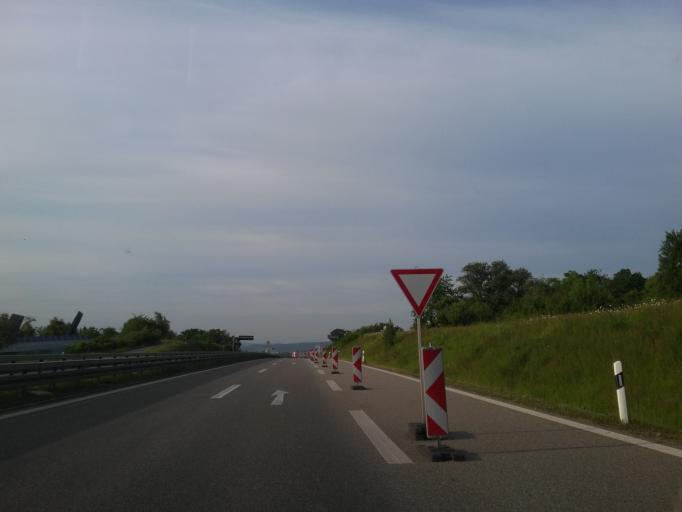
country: DE
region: Baden-Wuerttemberg
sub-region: Regierungsbezirk Stuttgart
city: Leutenbach
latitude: 48.9027
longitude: 9.4210
